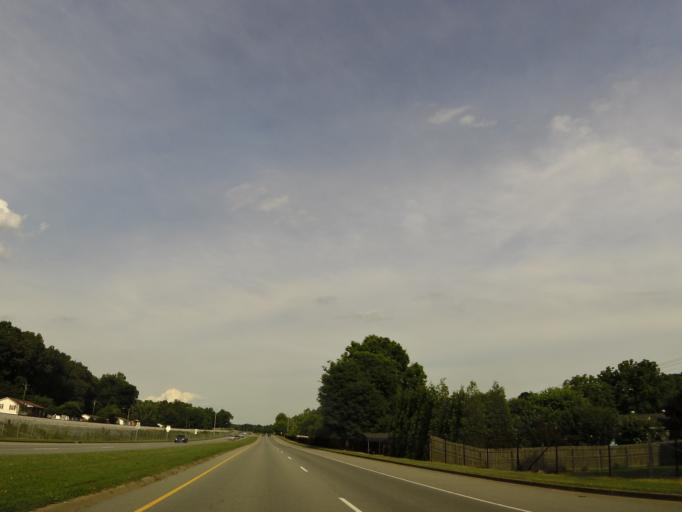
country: US
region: Tennessee
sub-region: Humphreys County
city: Waverly
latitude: 36.0859
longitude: -87.7873
